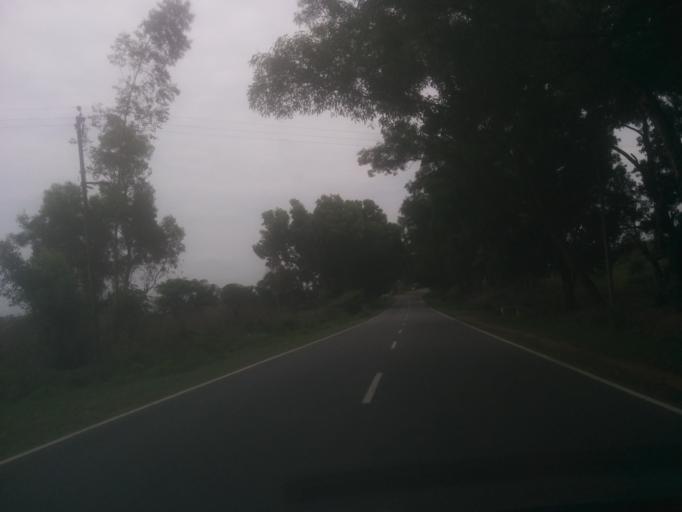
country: IN
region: Karnataka
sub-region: Hassan
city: Belur
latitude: 13.1604
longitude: 75.9024
